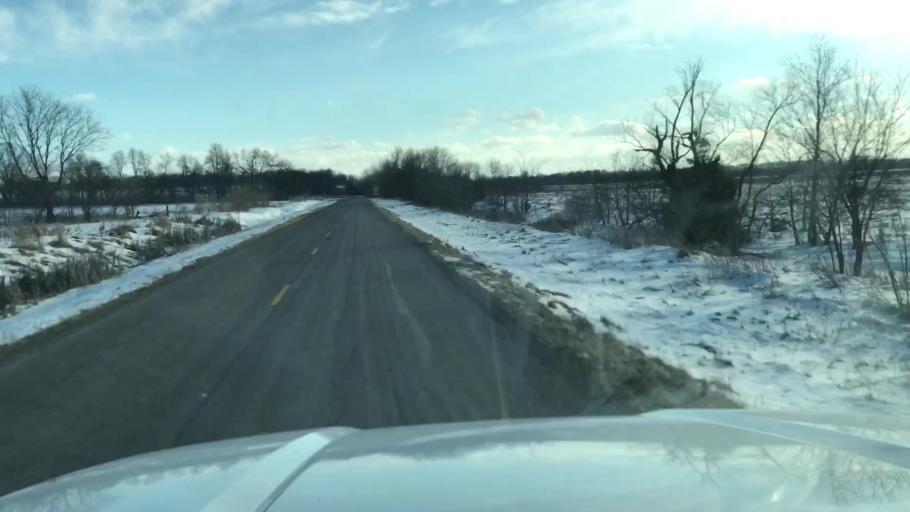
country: US
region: Missouri
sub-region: Holt County
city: Oregon
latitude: 40.1070
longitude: -95.0227
